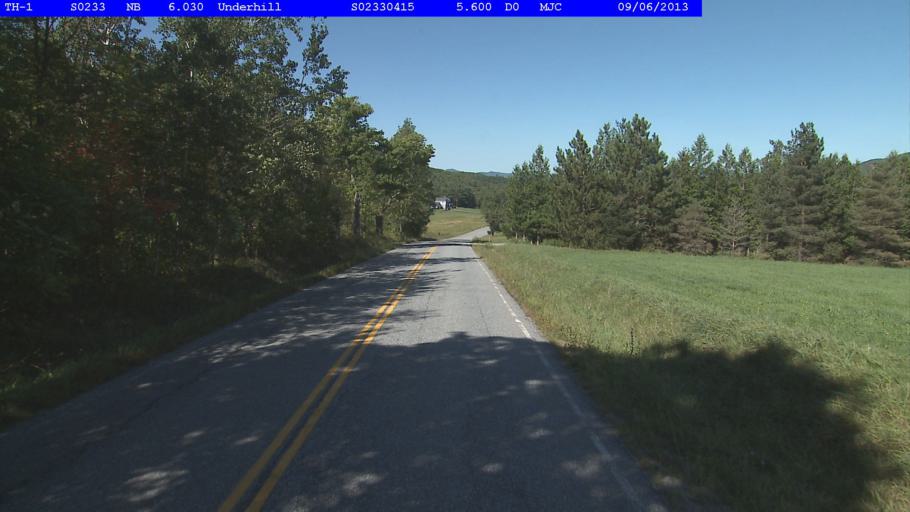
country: US
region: Vermont
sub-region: Chittenden County
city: Jericho
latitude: 44.5457
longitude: -72.8678
